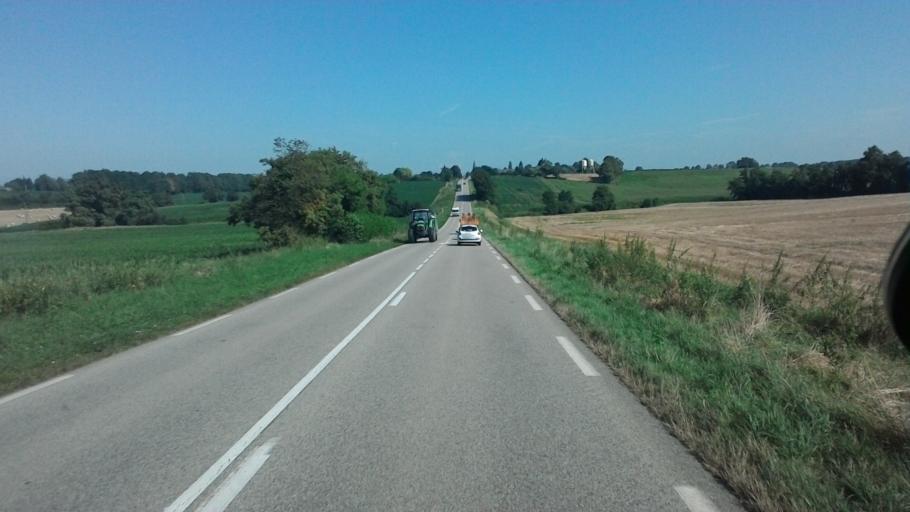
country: FR
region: Rhone-Alpes
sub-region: Departement de l'Ain
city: Saint-Trivier-de-Courtes
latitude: 46.4471
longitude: 5.0883
